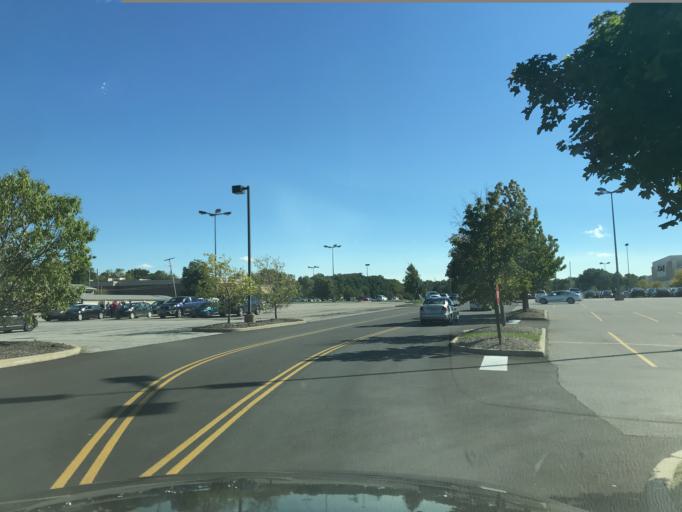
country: US
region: Ohio
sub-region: Lake County
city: Mentor
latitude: 41.6603
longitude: -81.3591
